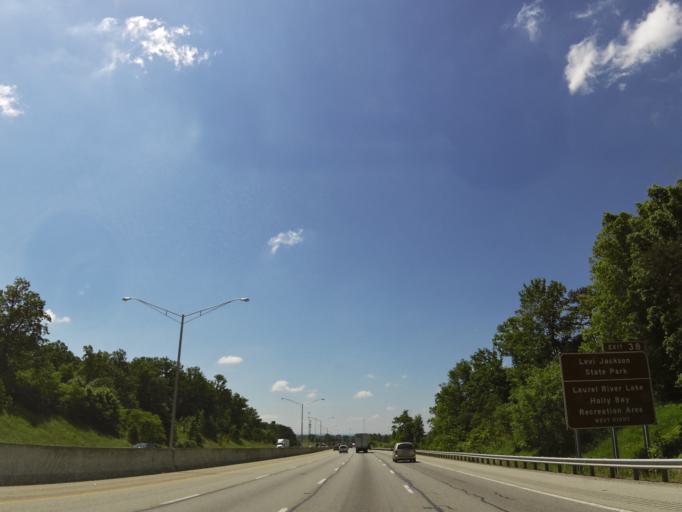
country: US
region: Kentucky
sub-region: Laurel County
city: London
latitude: 37.1184
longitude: -84.1055
